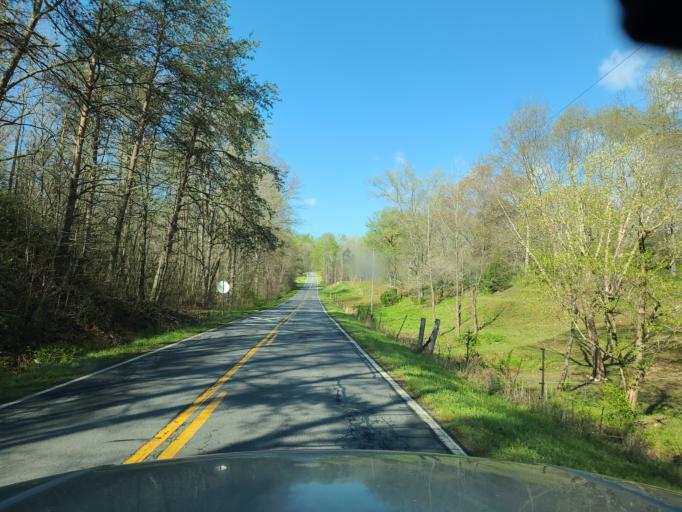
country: US
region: North Carolina
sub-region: Rutherford County
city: Forest City
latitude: 35.4039
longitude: -81.8739
